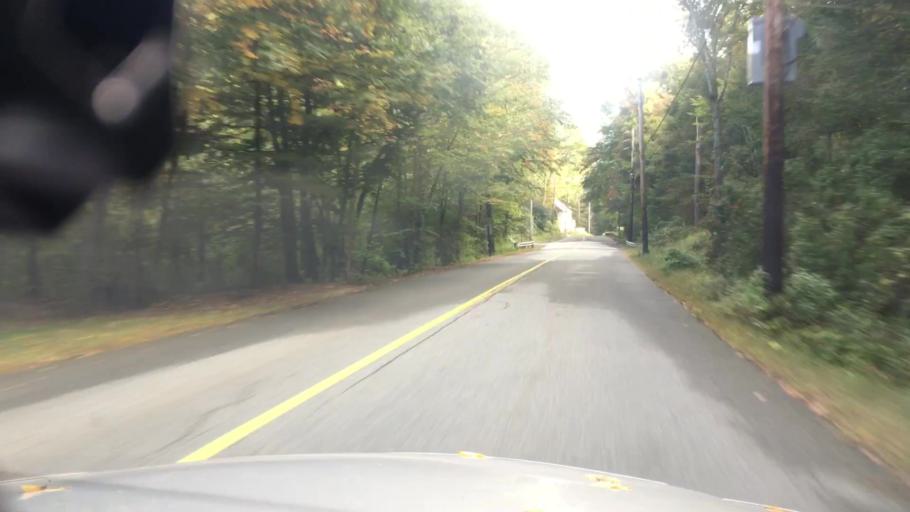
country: US
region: Connecticut
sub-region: Middlesex County
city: Essex Village
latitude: 41.3728
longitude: -72.4071
